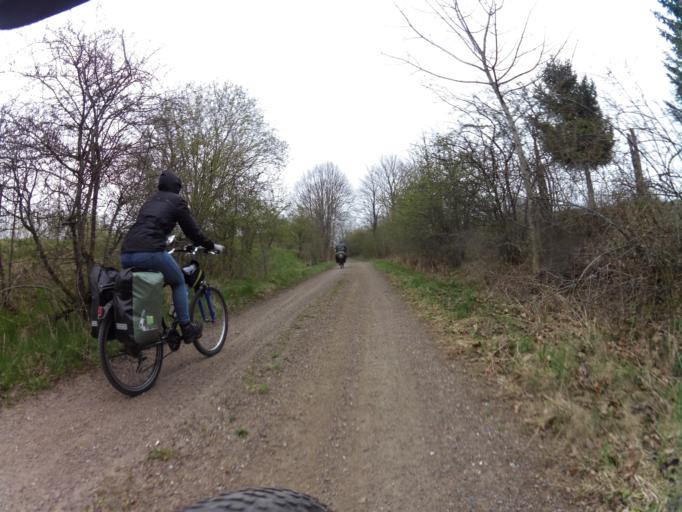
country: PL
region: West Pomeranian Voivodeship
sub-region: Powiat koszalinski
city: Bobolice
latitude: 53.9890
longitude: 16.6806
